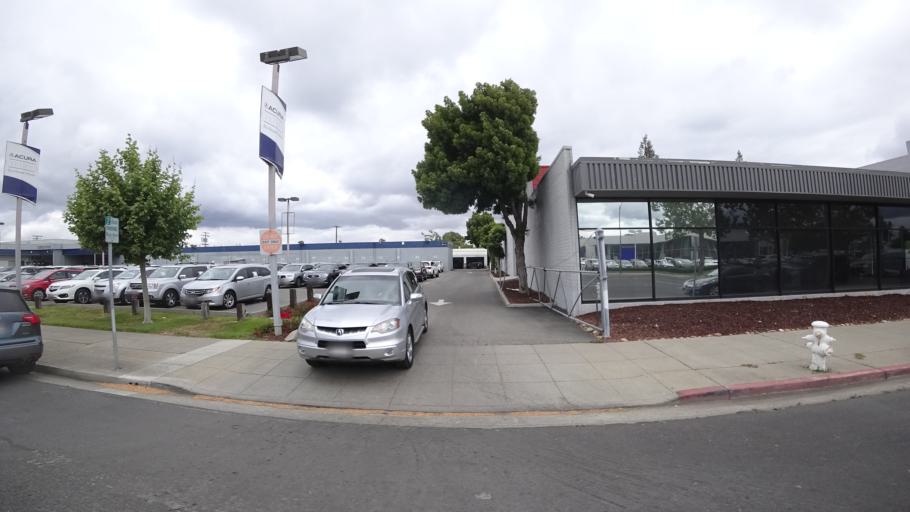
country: US
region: California
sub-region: Santa Clara County
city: Santa Clara
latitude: 37.3230
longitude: -121.9849
